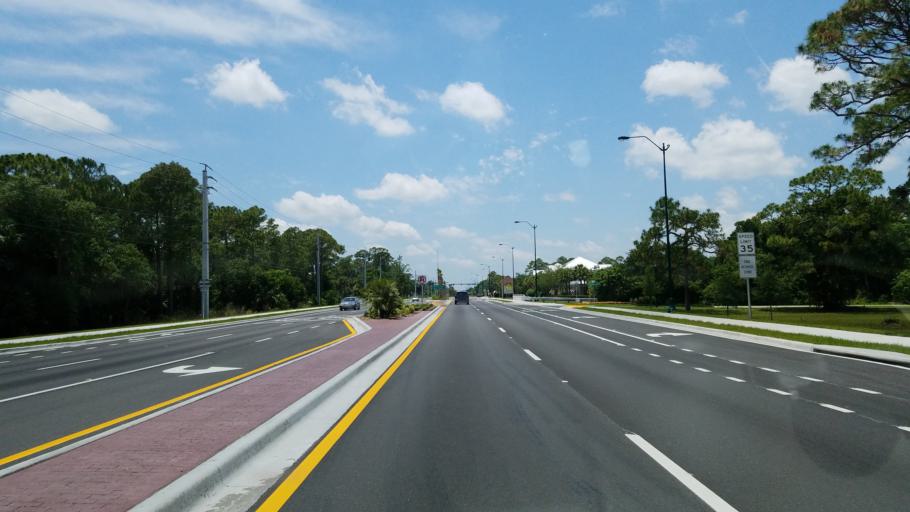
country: US
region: Florida
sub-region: Martin County
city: Palm City
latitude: 27.1613
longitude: -80.2822
